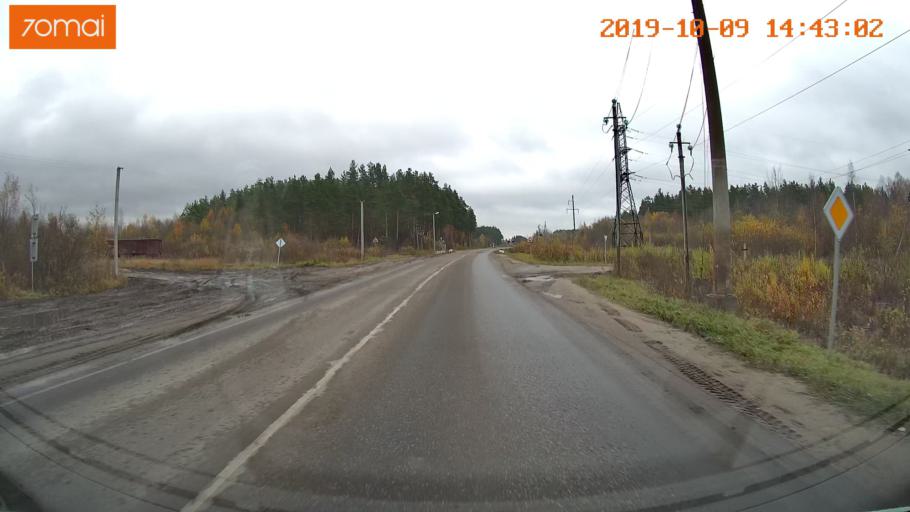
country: RU
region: Kostroma
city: Buy
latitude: 58.4586
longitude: 41.5405
